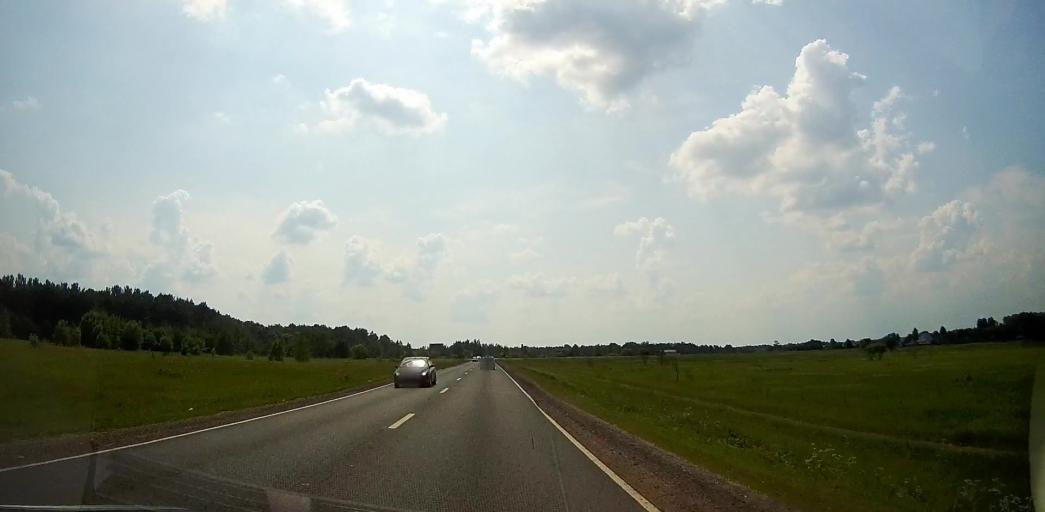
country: RU
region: Moskovskaya
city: Malino
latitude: 55.0989
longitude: 38.1678
